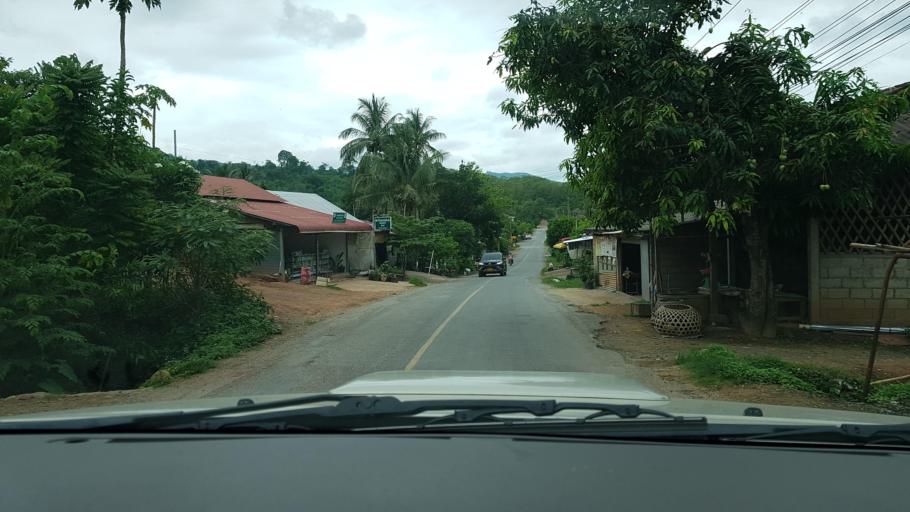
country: LA
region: Loungnamtha
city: Muang Nale
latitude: 20.3070
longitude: 101.6476
